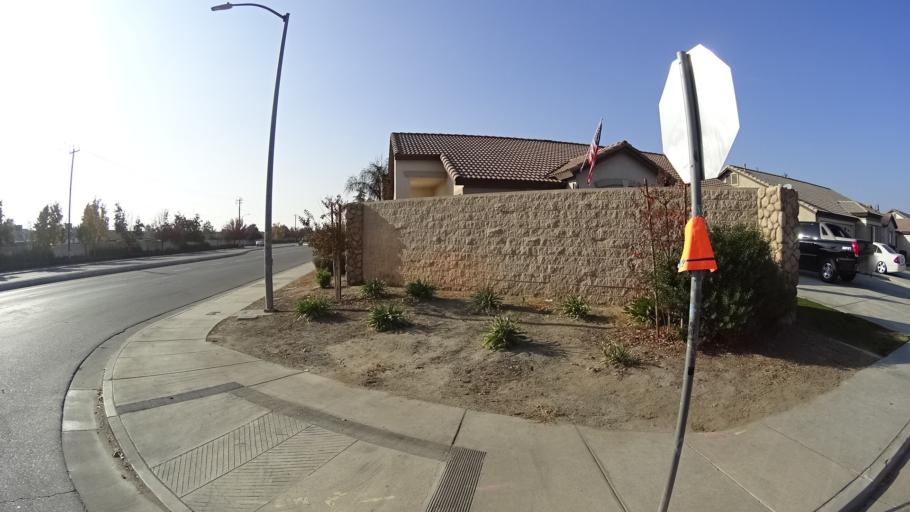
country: US
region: California
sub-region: Kern County
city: Greenfield
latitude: 35.2815
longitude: -119.0160
